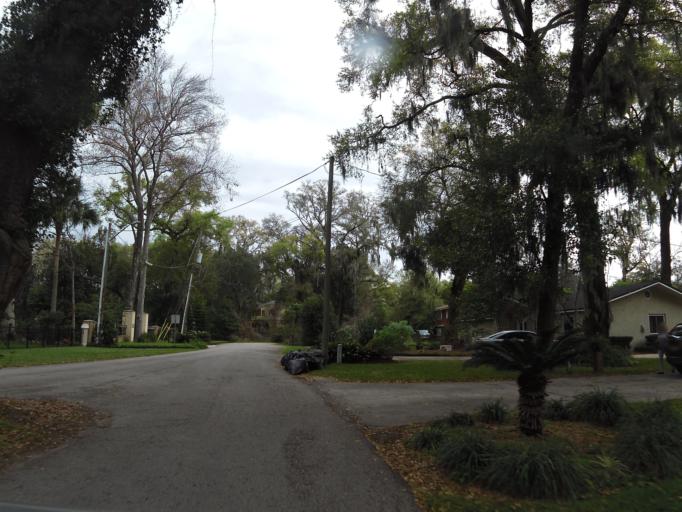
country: US
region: Florida
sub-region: Duval County
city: Jacksonville
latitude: 30.3387
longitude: -81.6082
